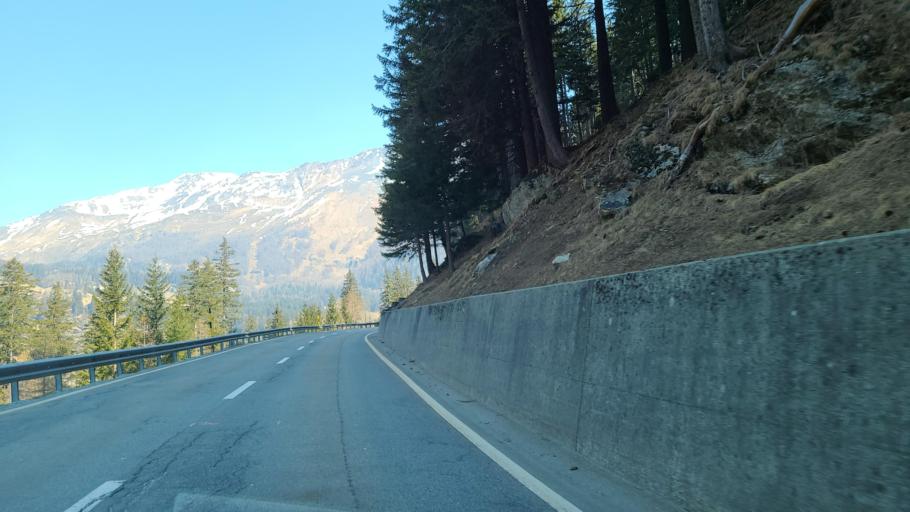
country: CH
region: Grisons
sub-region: Bernina District
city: Poschiavo
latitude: 46.3758
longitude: 10.0686
